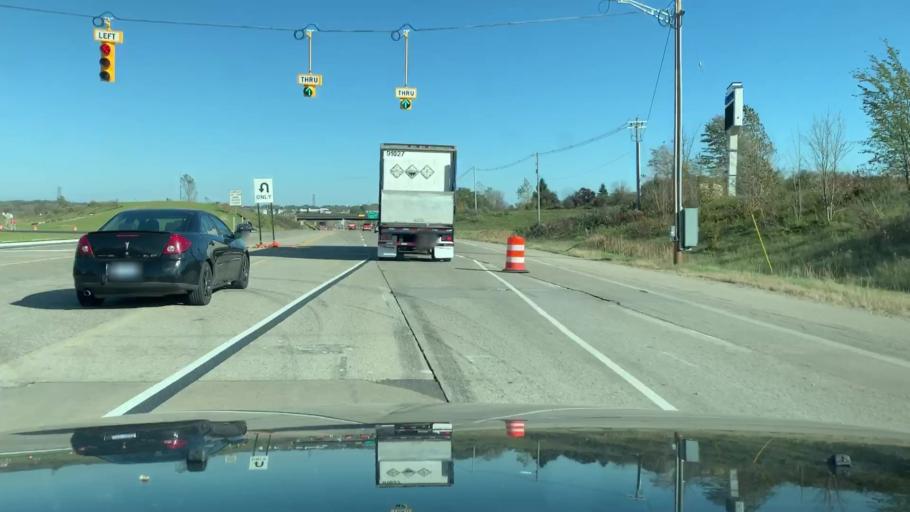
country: US
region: Michigan
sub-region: Ottawa County
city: Zeeland
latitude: 42.8122
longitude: -85.9857
